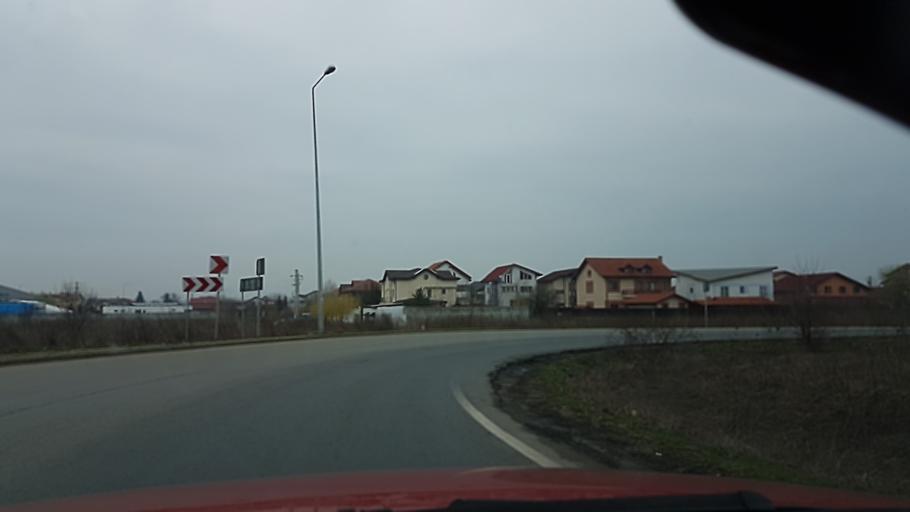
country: RO
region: Ilfov
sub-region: Comuna Tunari
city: Tunari
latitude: 44.5391
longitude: 26.1401
